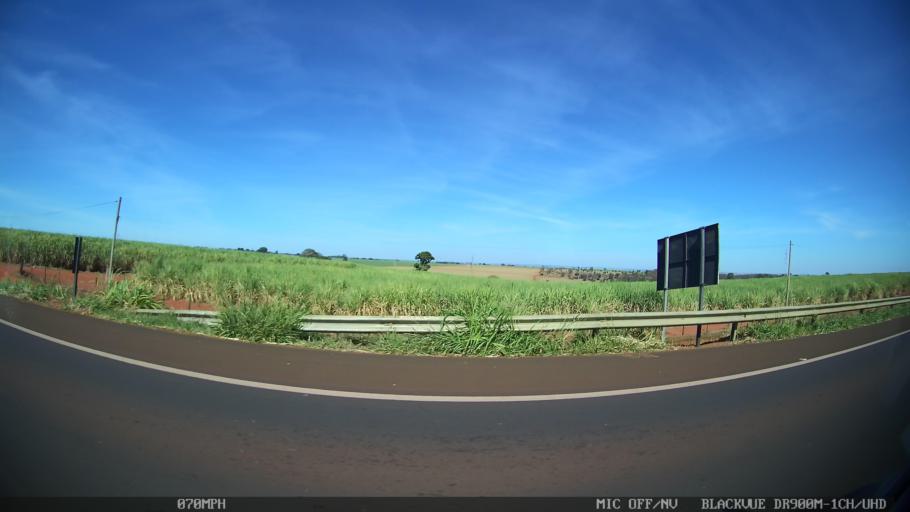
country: BR
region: Sao Paulo
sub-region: Franca
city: Franca
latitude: -20.5585
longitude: -47.5998
